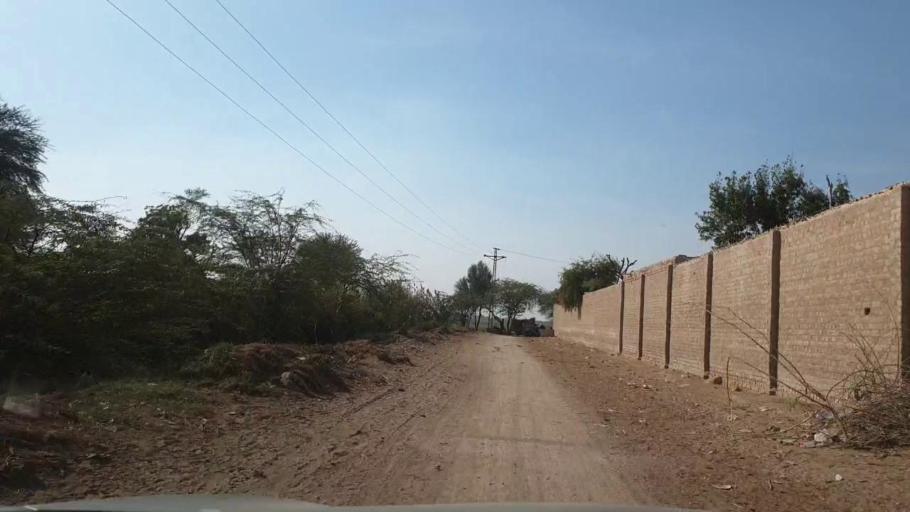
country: PK
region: Sindh
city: Berani
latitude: 25.7160
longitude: 68.7745
